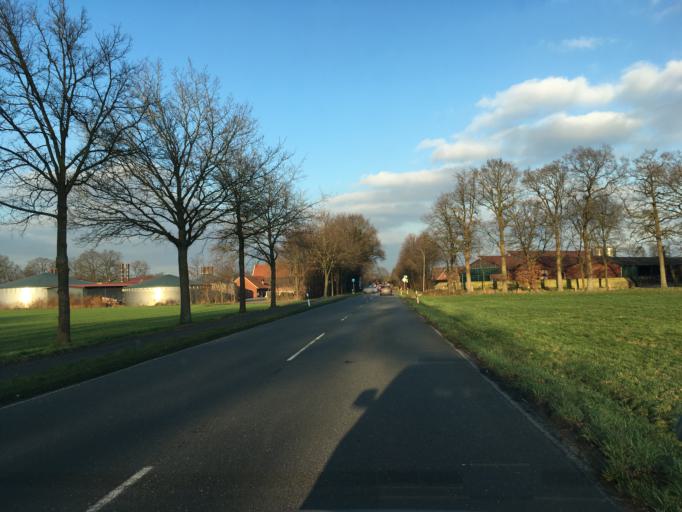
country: DE
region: North Rhine-Westphalia
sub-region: Regierungsbezirk Munster
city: Gronau
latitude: 52.1659
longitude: 7.0308
